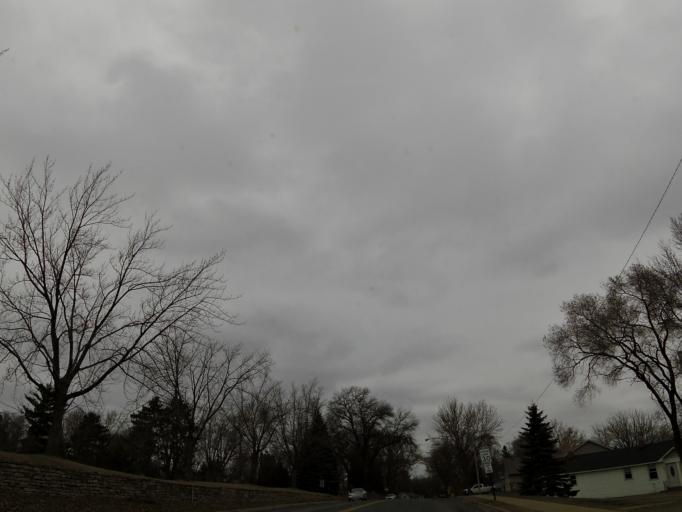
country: US
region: Minnesota
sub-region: Washington County
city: Bayport
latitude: 45.0219
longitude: -92.7843
